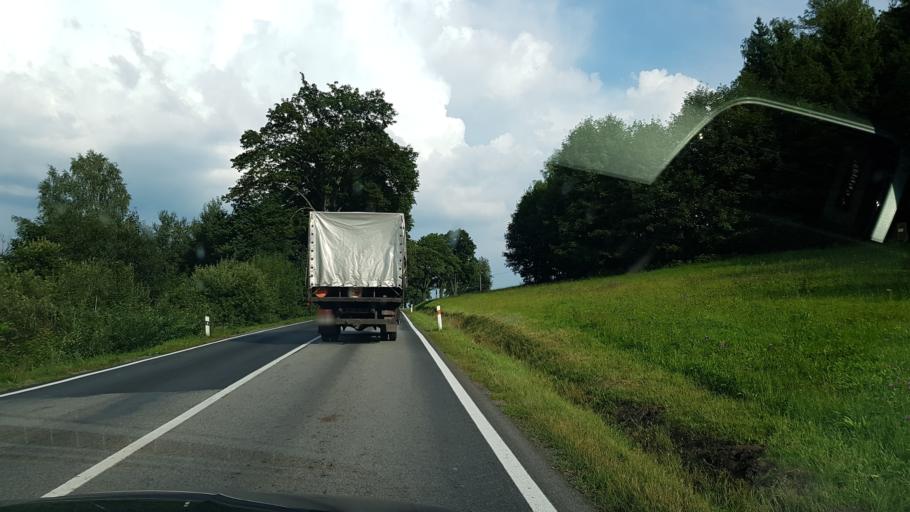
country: PL
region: Lower Silesian Voivodeship
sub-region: Powiat klodzki
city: Miedzylesie
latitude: 50.0994
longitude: 16.6335
